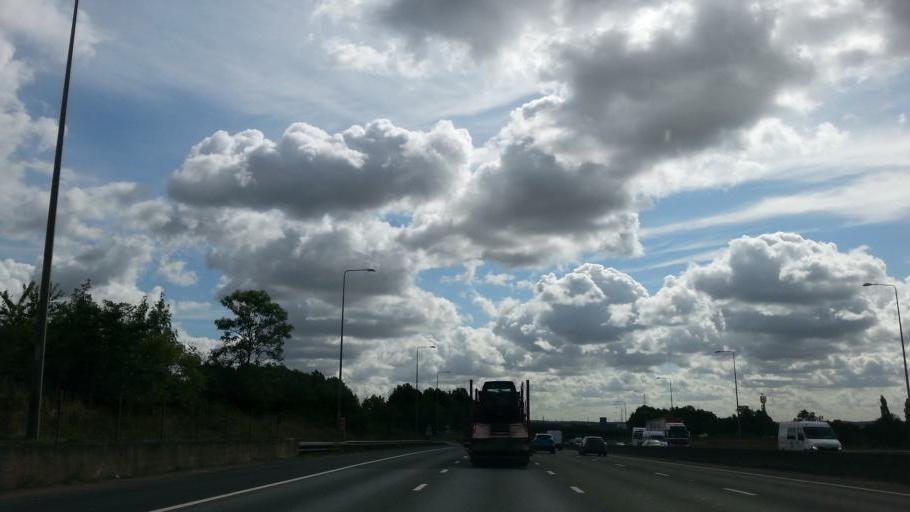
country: GB
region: England
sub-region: Essex
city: Epping
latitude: 51.6691
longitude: 0.1536
